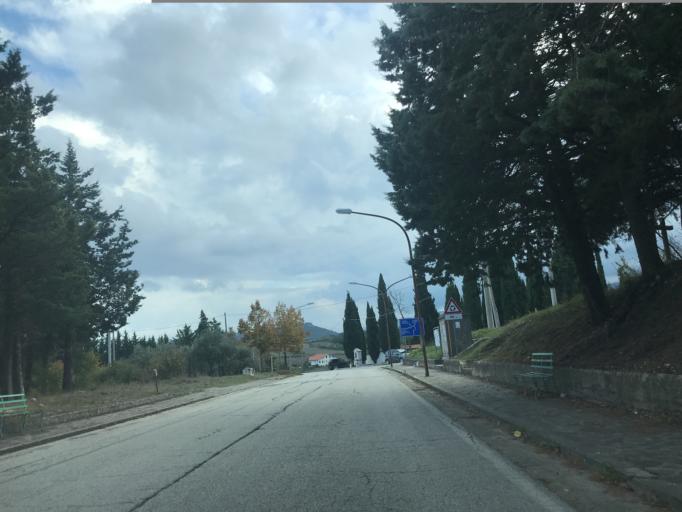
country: IT
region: Molise
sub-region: Provincia di Isernia
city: Bagnoli del Trigno
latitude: 41.6983
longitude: 14.4605
